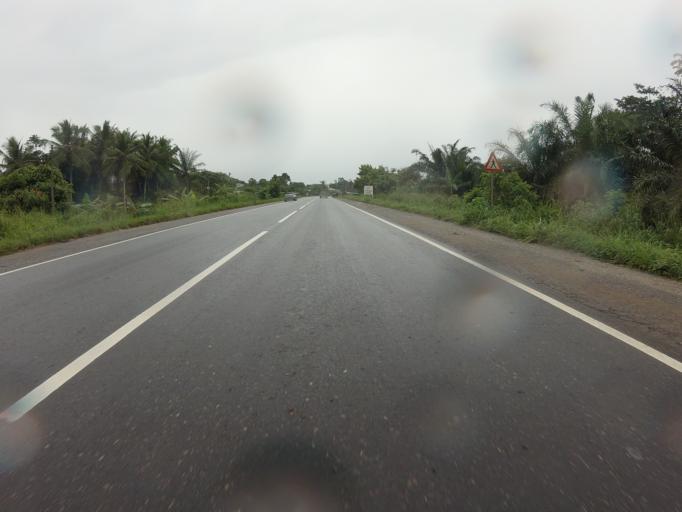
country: GH
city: Kibi
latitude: 6.1573
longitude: -0.4831
